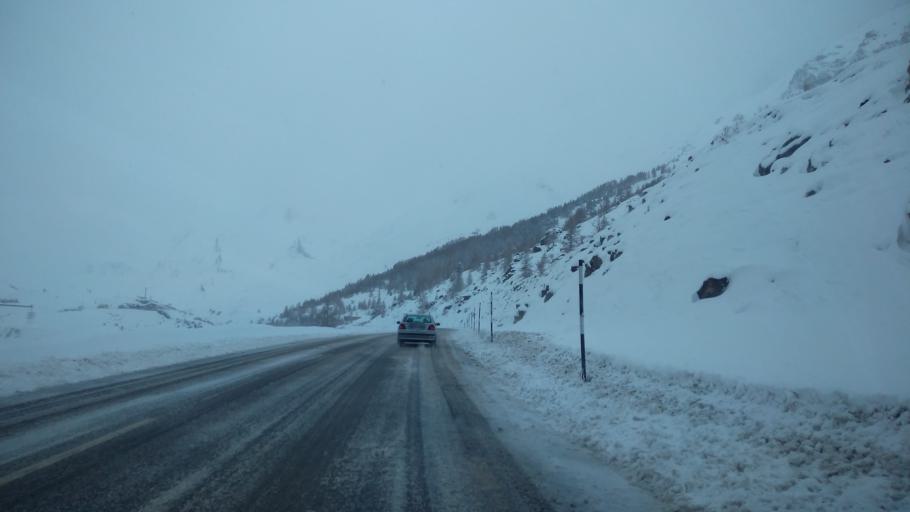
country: FR
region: Provence-Alpes-Cote d'Azur
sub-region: Departement des Hautes-Alpes
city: Le Monetier-les-Bains
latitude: 45.0338
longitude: 6.4388
